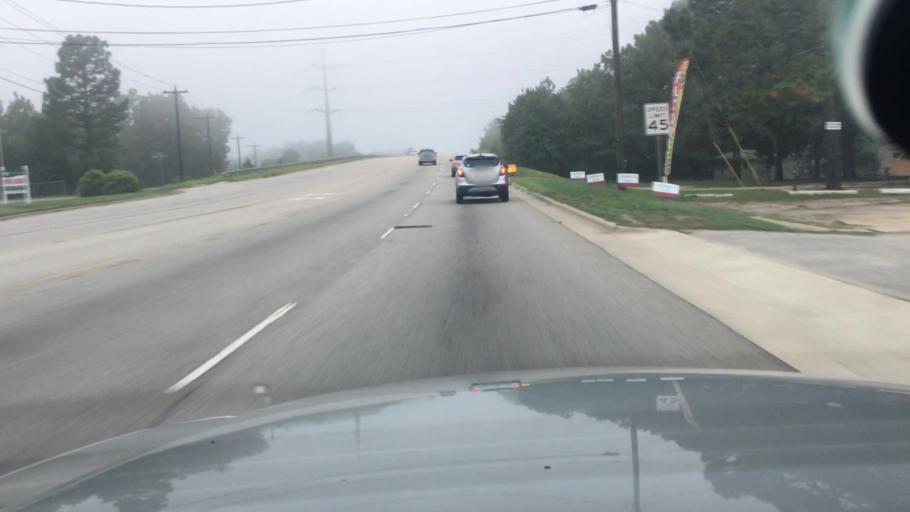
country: US
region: North Carolina
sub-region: Cumberland County
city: Hope Mills
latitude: 35.0180
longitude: -78.9202
